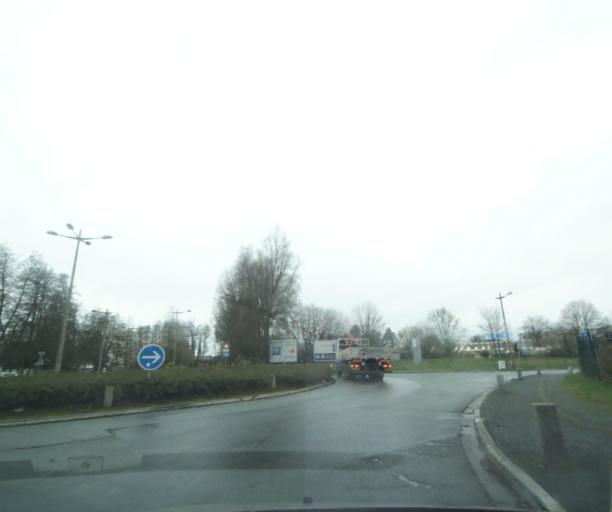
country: FR
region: Nord-Pas-de-Calais
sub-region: Departement du Nord
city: Prouvy
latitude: 50.3352
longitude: 3.4550
